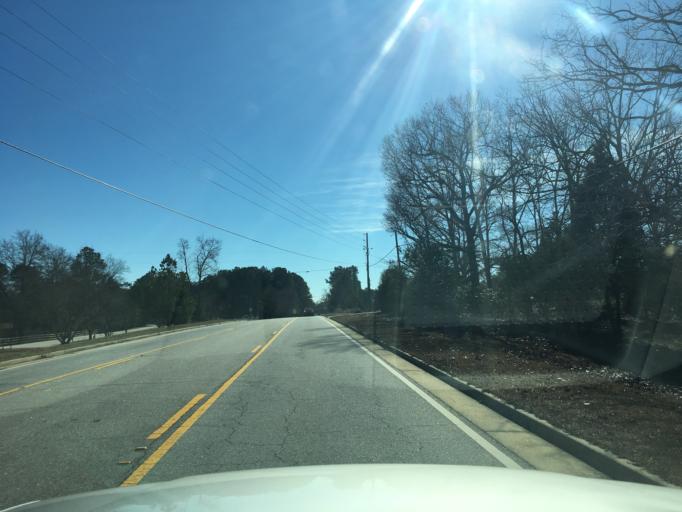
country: US
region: Georgia
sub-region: Rockdale County
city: Conyers
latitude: 33.6553
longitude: -84.0502
